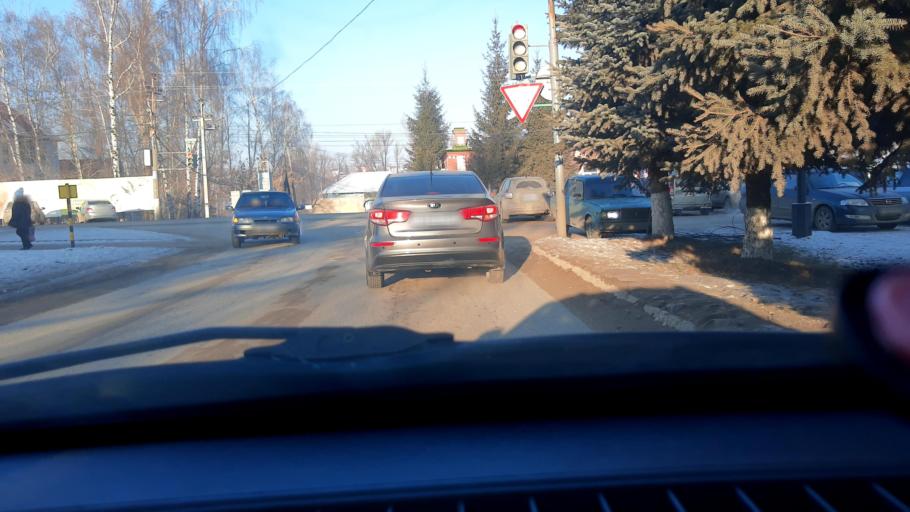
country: RU
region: Bashkortostan
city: Iglino
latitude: 54.8346
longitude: 56.4159
